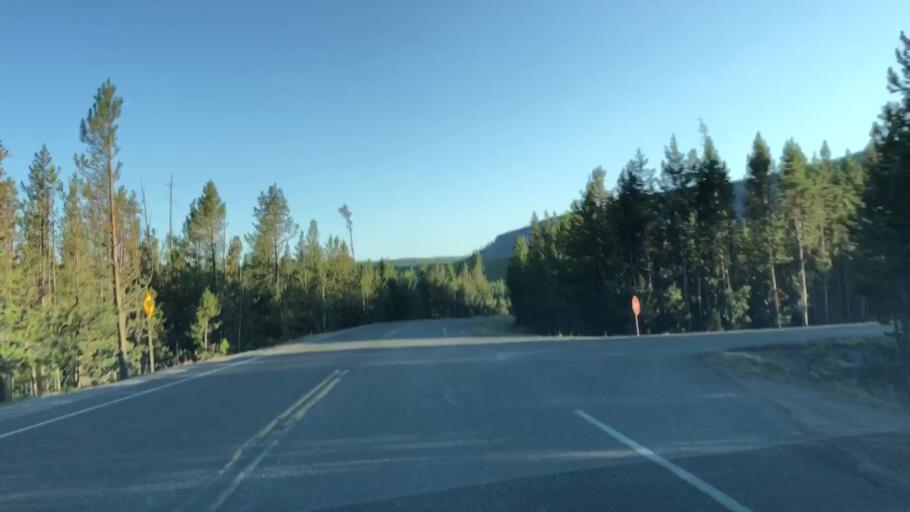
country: US
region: Montana
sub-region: Gallatin County
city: West Yellowstone
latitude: 44.6436
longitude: -110.8592
